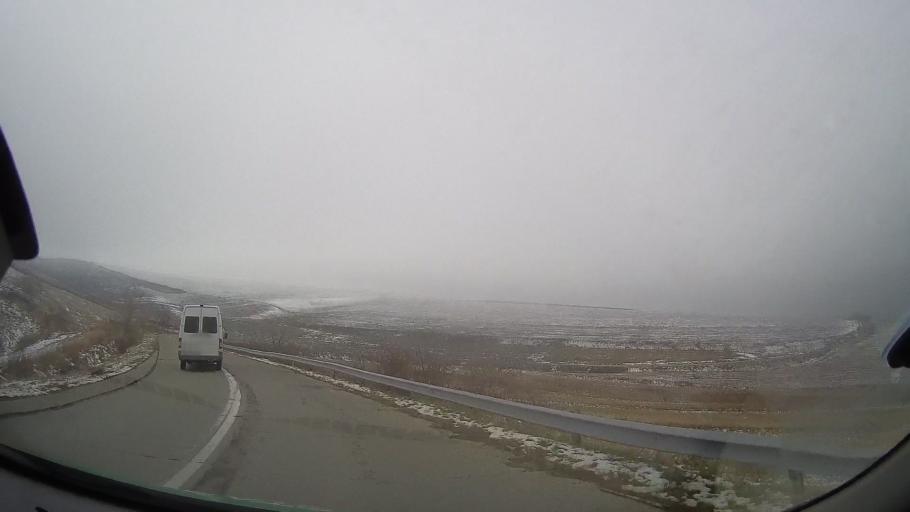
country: RO
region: Vaslui
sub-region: Comuna Grivita
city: Grivita
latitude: 46.1943
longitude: 27.6051
